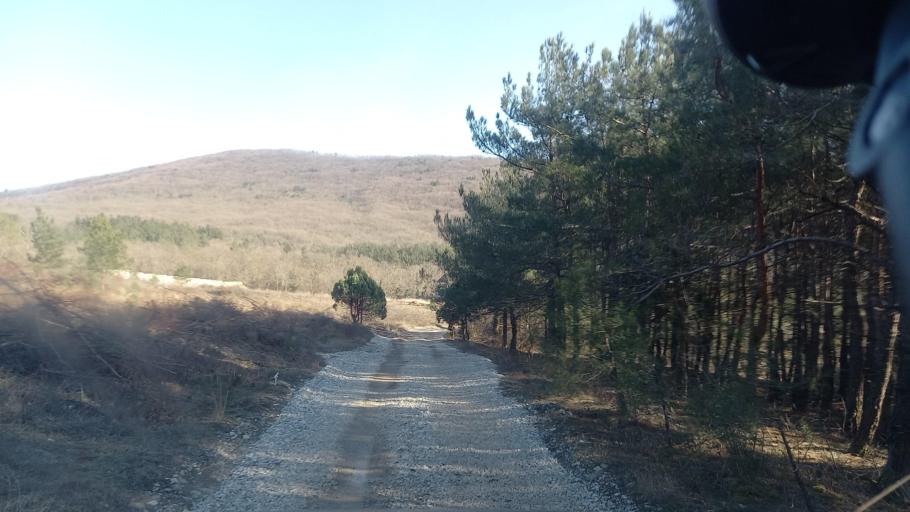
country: RU
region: Krasnodarskiy
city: Kabardinka
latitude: 44.6289
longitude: 37.9308
